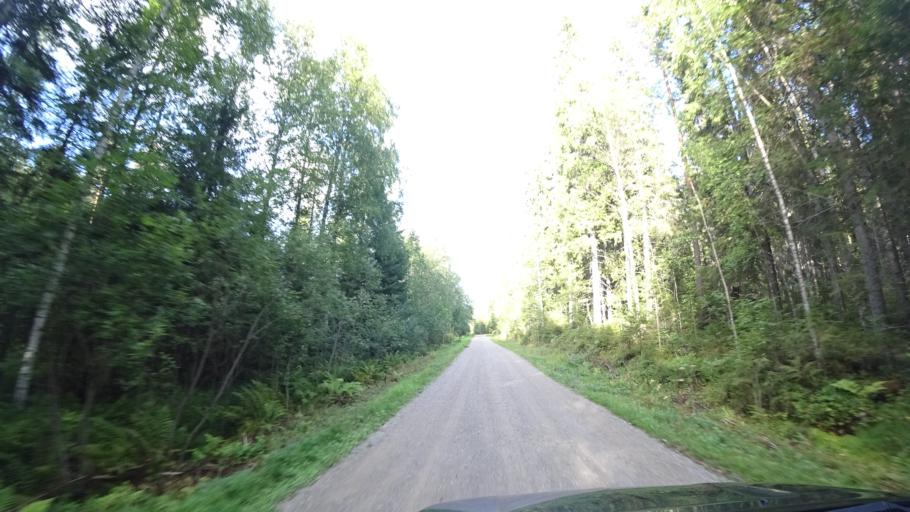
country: FI
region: Paijanne Tavastia
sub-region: Lahti
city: Auttoinen
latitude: 61.2200
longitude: 25.1796
